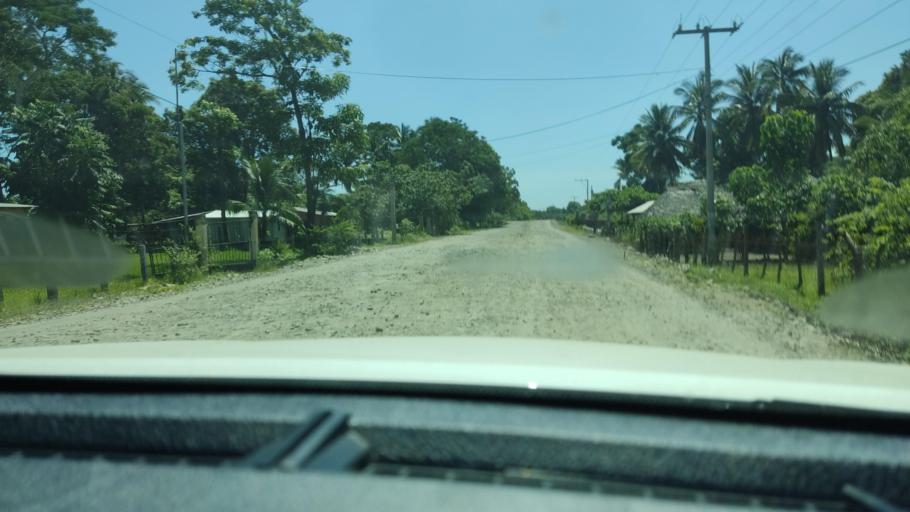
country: SV
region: Ahuachapan
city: San Francisco Menendez
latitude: 13.7518
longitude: -90.1236
